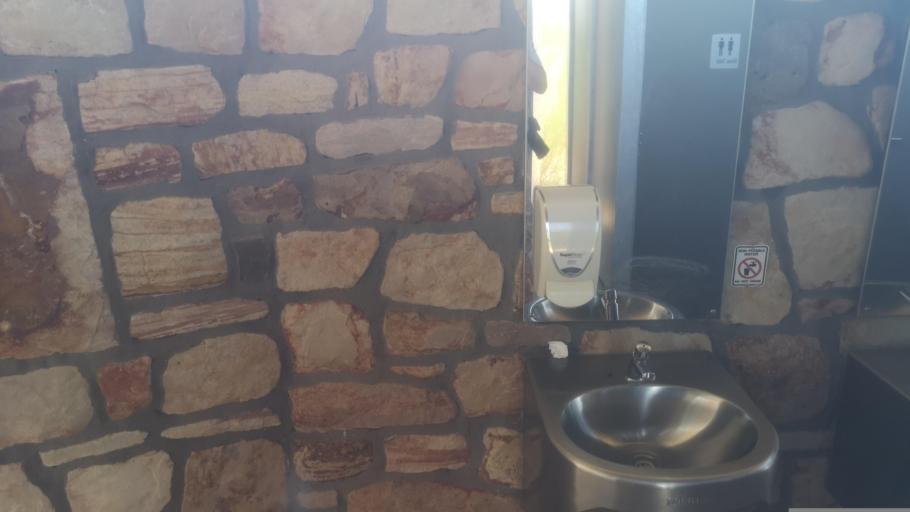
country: AU
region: Western Australia
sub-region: Northampton Shire
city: Kalbarri
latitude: -27.5546
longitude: 114.4334
